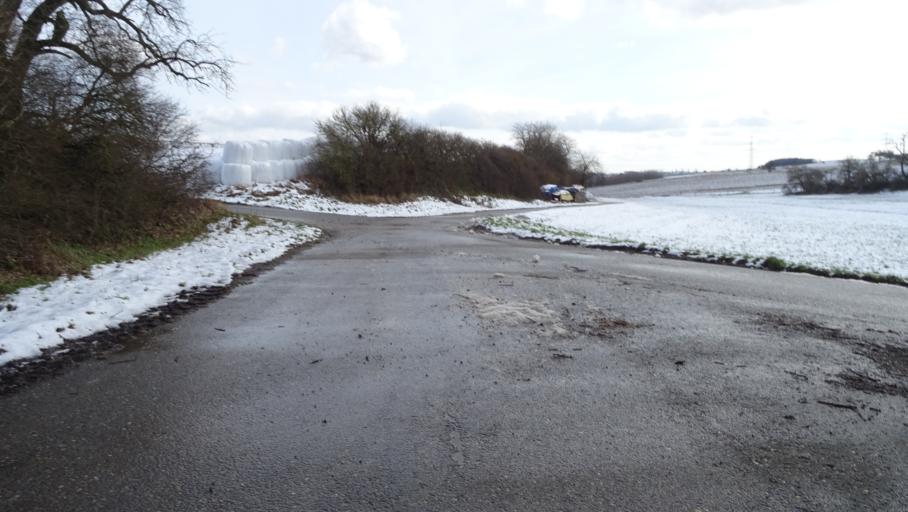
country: DE
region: Baden-Wuerttemberg
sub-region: Karlsruhe Region
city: Limbach
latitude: 49.4276
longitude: 9.2682
